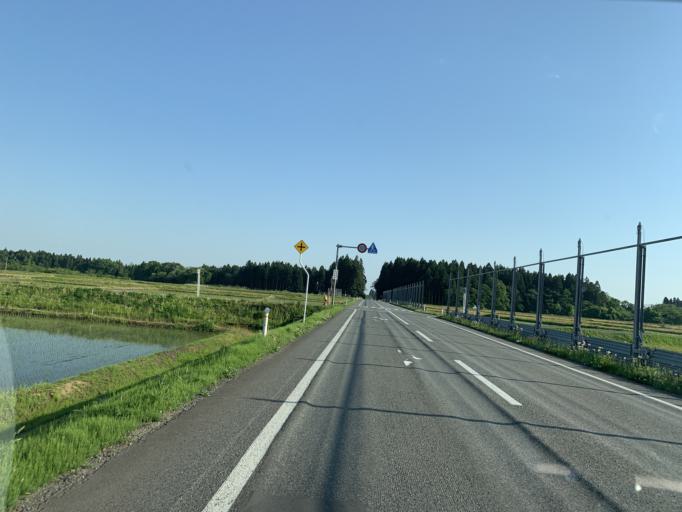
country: JP
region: Iwate
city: Kitakami
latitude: 39.2256
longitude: 141.0547
